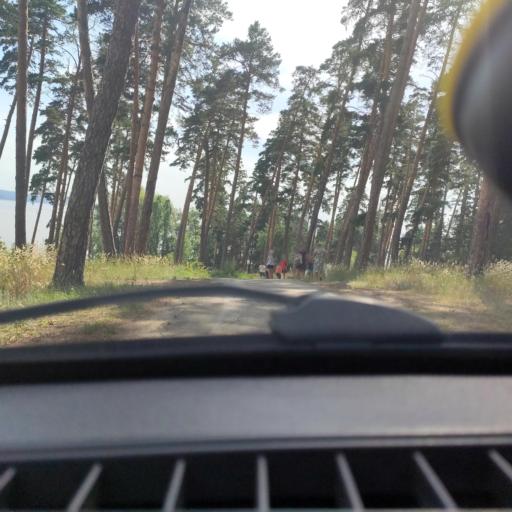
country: RU
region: Samara
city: Tol'yatti
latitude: 53.4739
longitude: 49.3422
